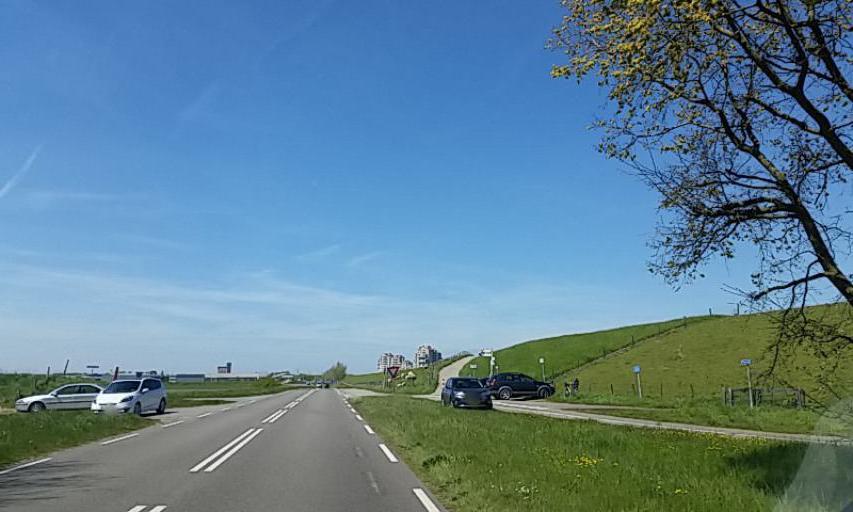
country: NL
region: Zeeland
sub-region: Gemeente Vlissingen
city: Vlissingen
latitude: 51.3868
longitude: 3.5849
